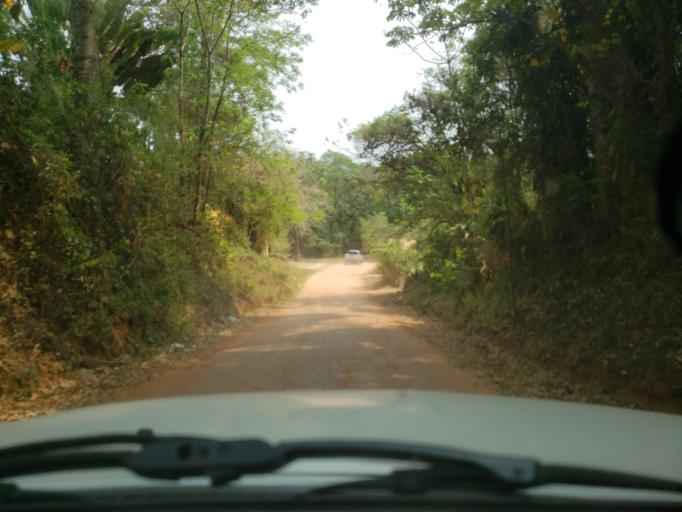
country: BR
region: Minas Gerais
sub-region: Jacutinga
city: Jacutinga
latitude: -22.3098
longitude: -46.6055
